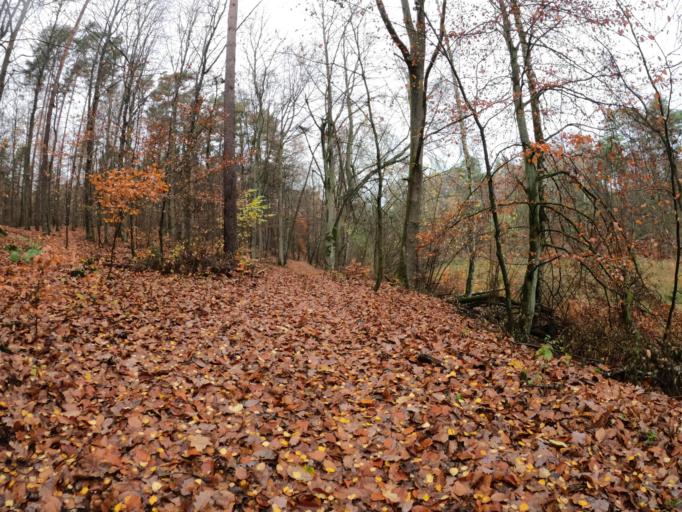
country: PL
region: West Pomeranian Voivodeship
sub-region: Powiat walecki
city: Tuczno
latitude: 53.2674
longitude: 16.2547
